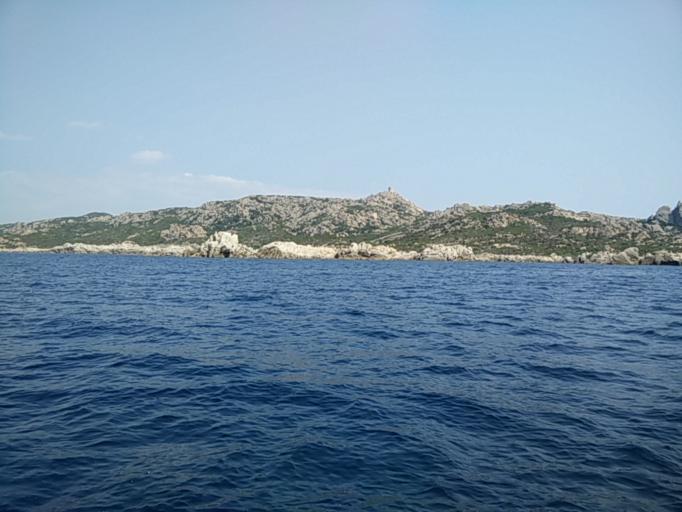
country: FR
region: Corsica
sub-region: Departement de la Corse-du-Sud
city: Propriano
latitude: 41.5672
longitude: 8.7858
